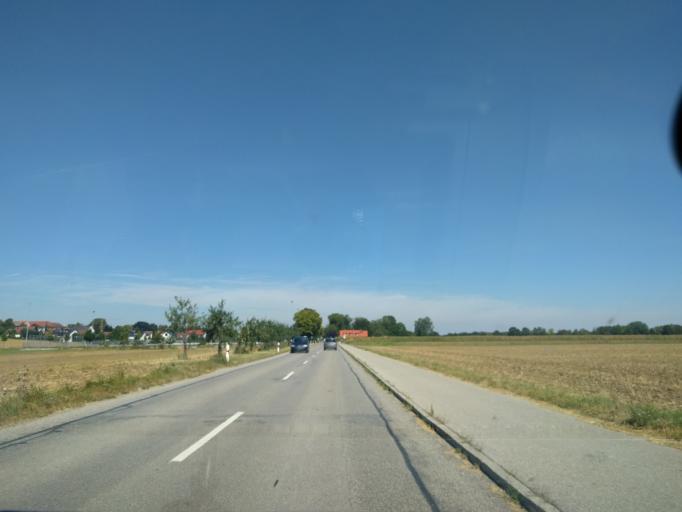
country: DE
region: Bavaria
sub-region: Upper Bavaria
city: Fuerstenfeldbruck
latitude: 48.1832
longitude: 11.2249
